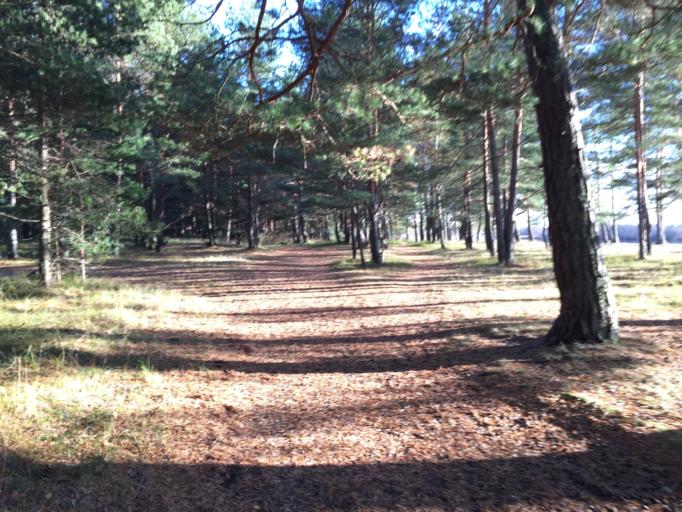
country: LV
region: Carnikava
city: Carnikava
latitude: 57.1562
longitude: 24.2741
